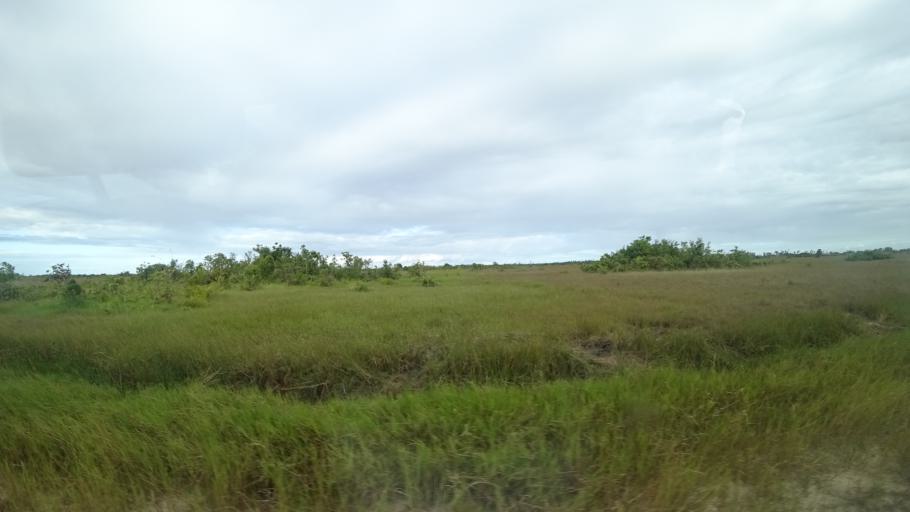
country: MZ
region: Sofala
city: Beira
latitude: -19.7019
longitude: 35.0248
